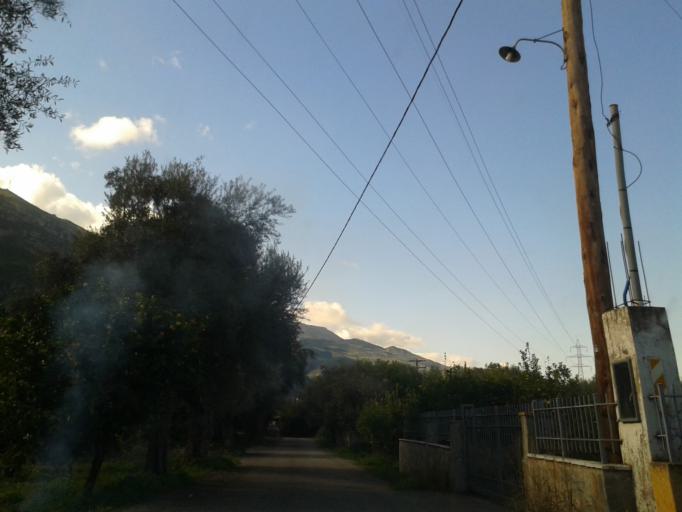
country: GR
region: West Greece
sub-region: Nomos Achaias
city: Temeni
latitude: 38.1893
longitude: 22.1846
